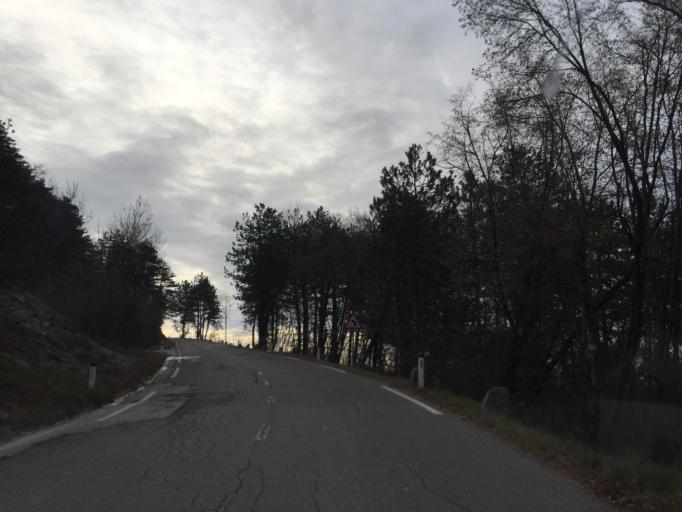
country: SI
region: Nova Gorica
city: Kromberk
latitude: 45.9871
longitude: 13.7053
